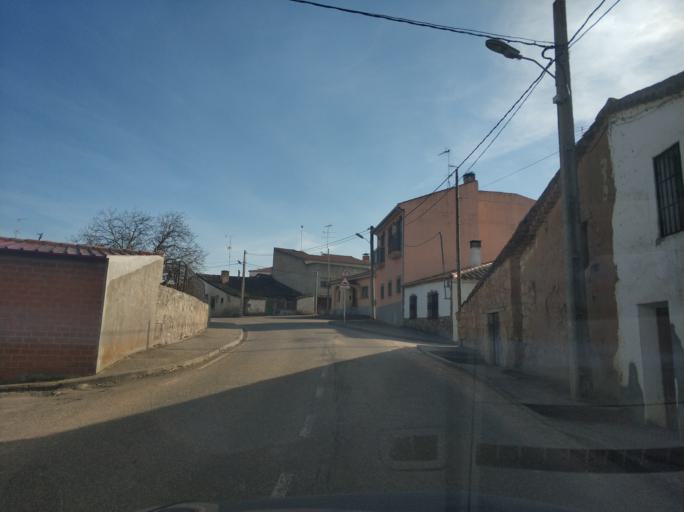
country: ES
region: Castille and Leon
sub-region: Provincia de Salamanca
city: Florida de Liebana
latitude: 41.0264
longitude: -5.7605
